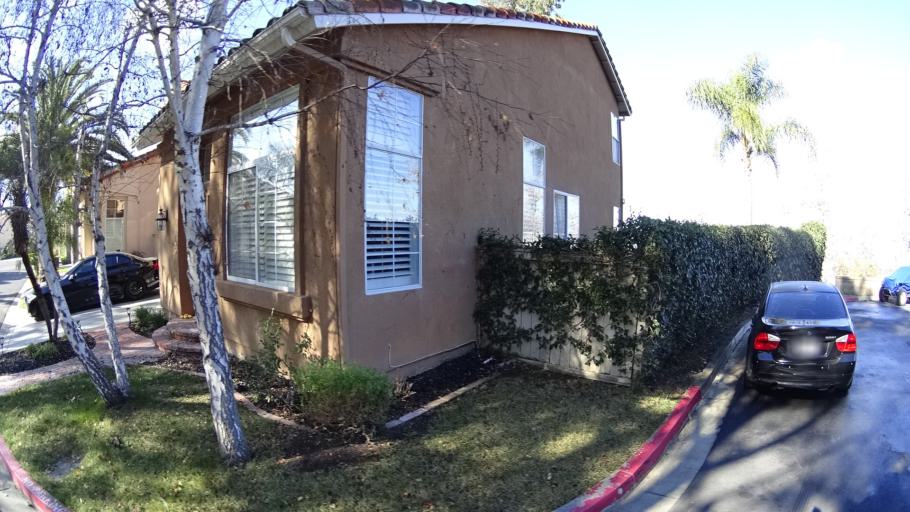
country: US
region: California
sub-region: Orange County
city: Laguna Woods
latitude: 33.6051
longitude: -117.7356
